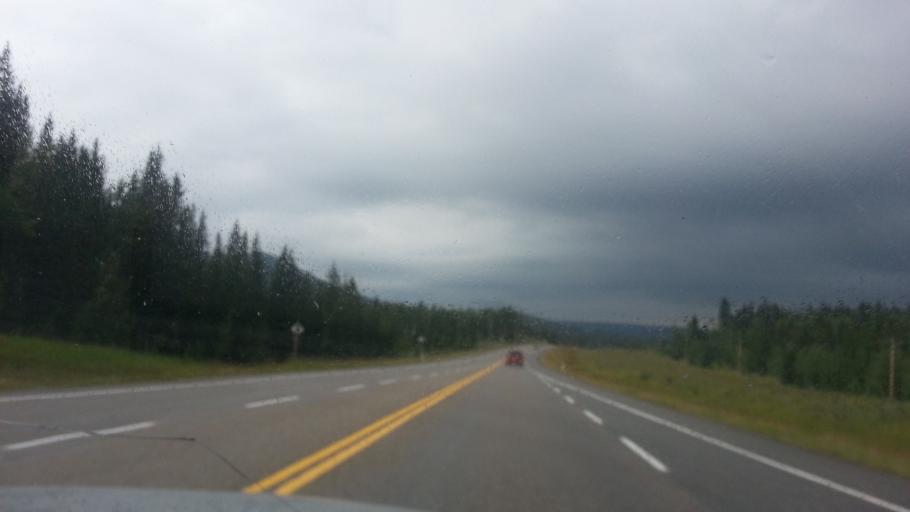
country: CA
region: Alberta
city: Cochrane
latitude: 50.9437
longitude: -114.5603
